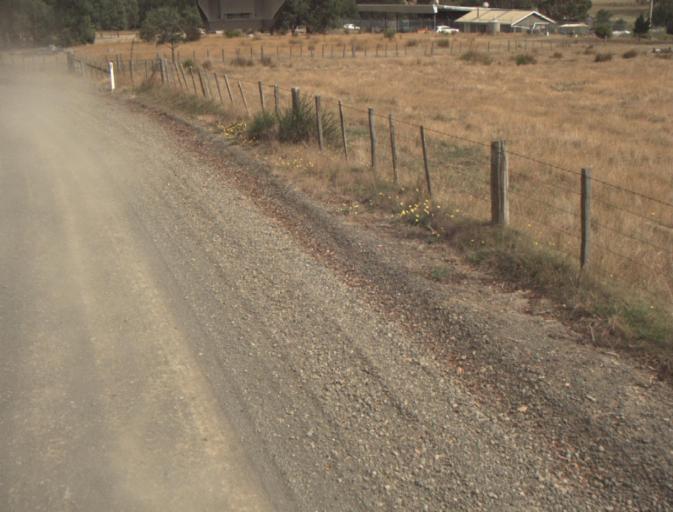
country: AU
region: Tasmania
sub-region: Dorset
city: Scottsdale
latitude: -41.4712
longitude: 147.5749
